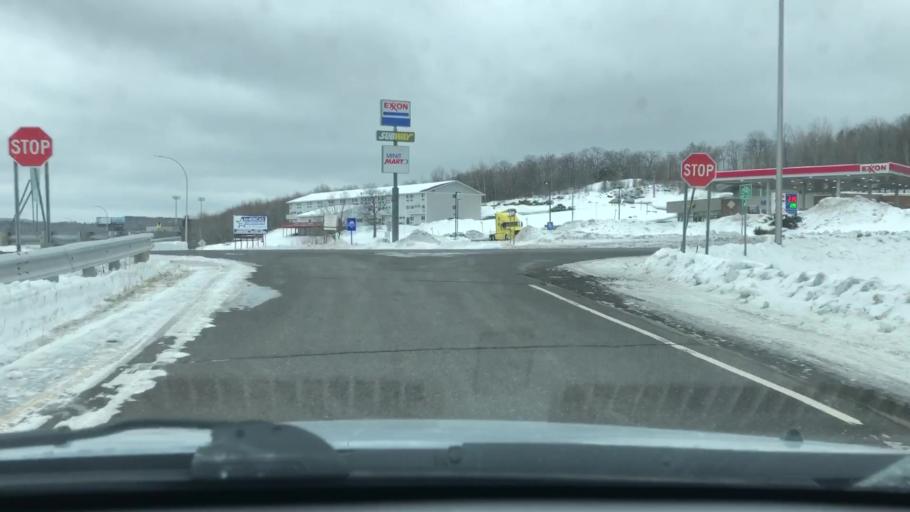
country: US
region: Minnesota
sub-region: Saint Louis County
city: Proctor
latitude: 46.7266
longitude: -92.2168
